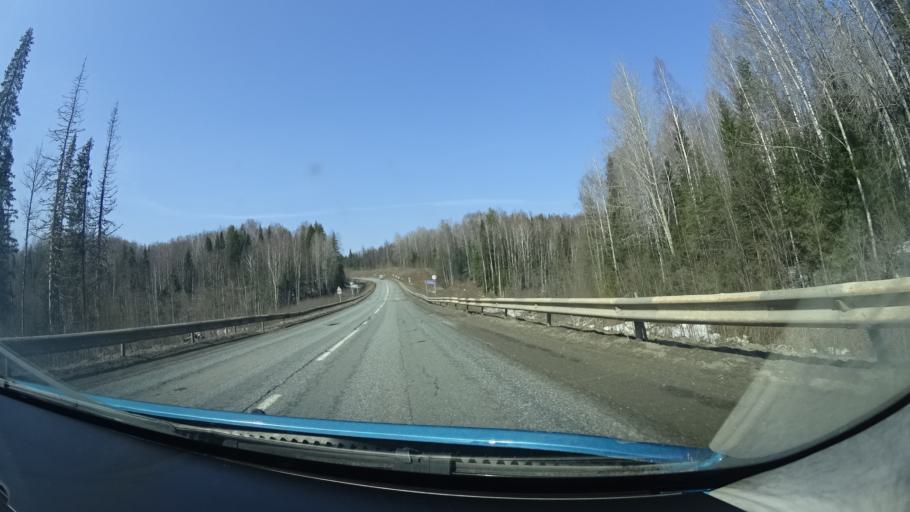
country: RU
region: Perm
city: Yugo-Kamskiy
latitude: 57.5923
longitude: 55.6651
